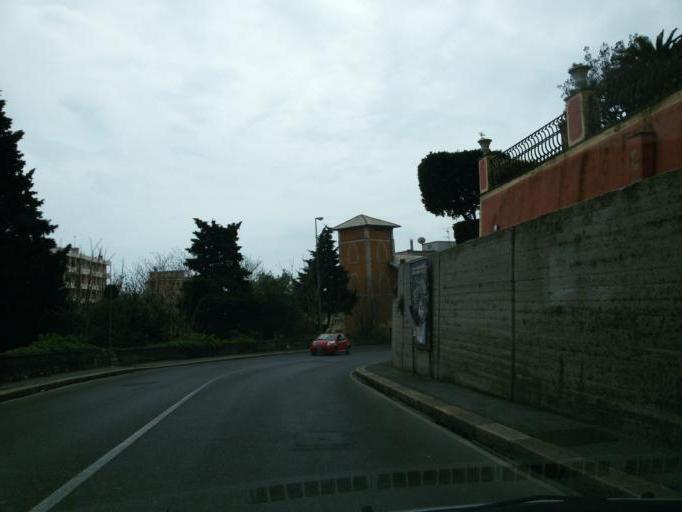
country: IT
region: Liguria
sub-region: Provincia di Genova
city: Genoa
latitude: 44.4008
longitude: 8.9795
